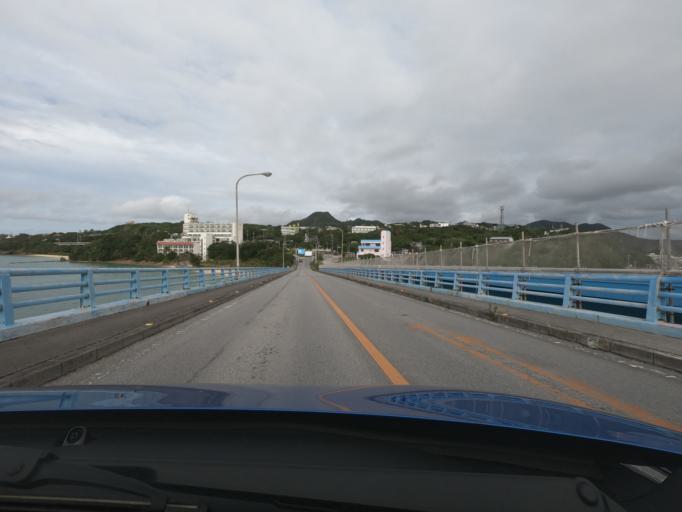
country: JP
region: Okinawa
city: Nago
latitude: 26.6612
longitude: 127.8894
